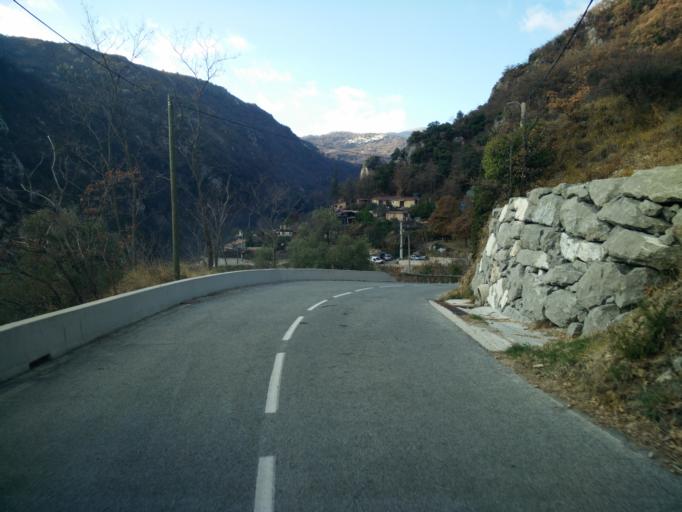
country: FR
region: Provence-Alpes-Cote d'Azur
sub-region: Departement des Alpes-Maritimes
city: Le Broc
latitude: 43.8186
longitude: 7.1218
